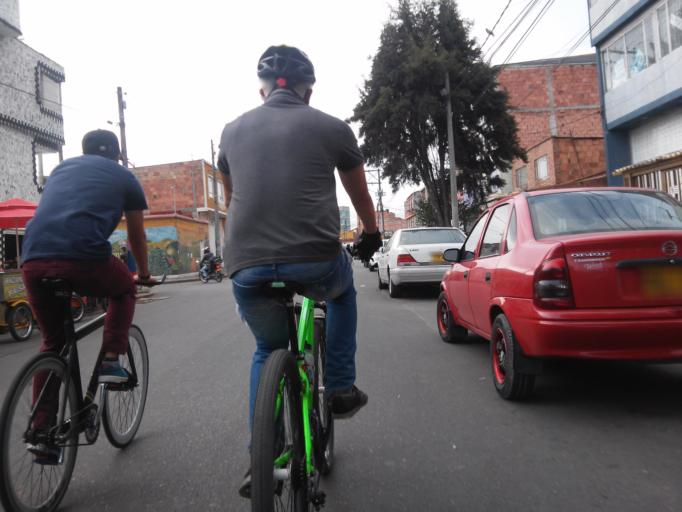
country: CO
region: Bogota D.C.
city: Bogota
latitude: 4.6170
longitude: -74.1456
